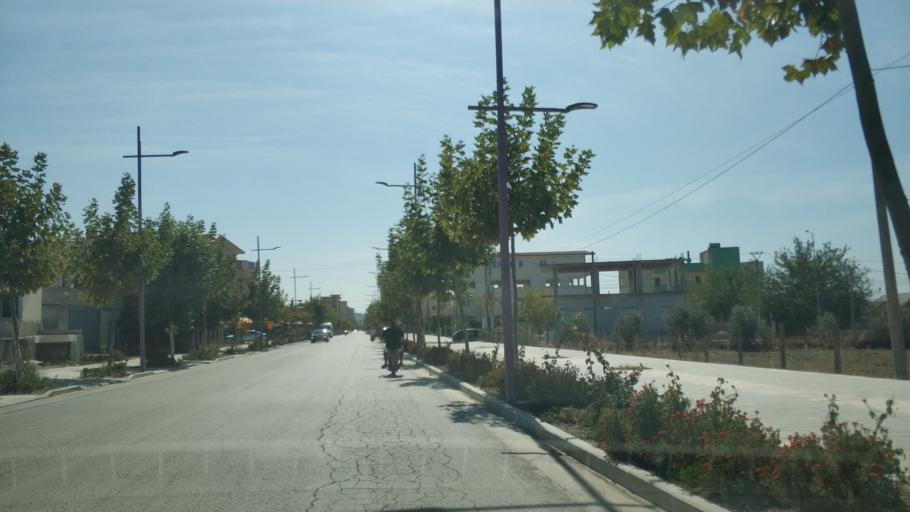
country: AL
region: Fier
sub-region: Rrethi i Lushnjes
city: Divjake
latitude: 41.0033
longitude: 19.5298
